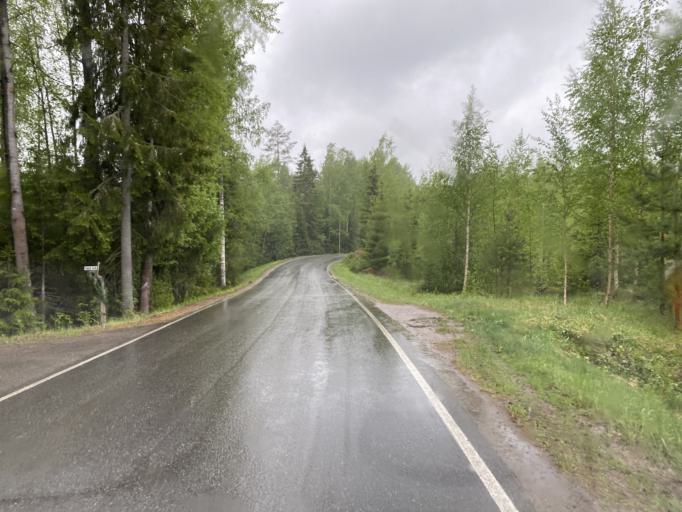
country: FI
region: Haeme
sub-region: Forssa
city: Humppila
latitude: 61.0914
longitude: 23.3130
